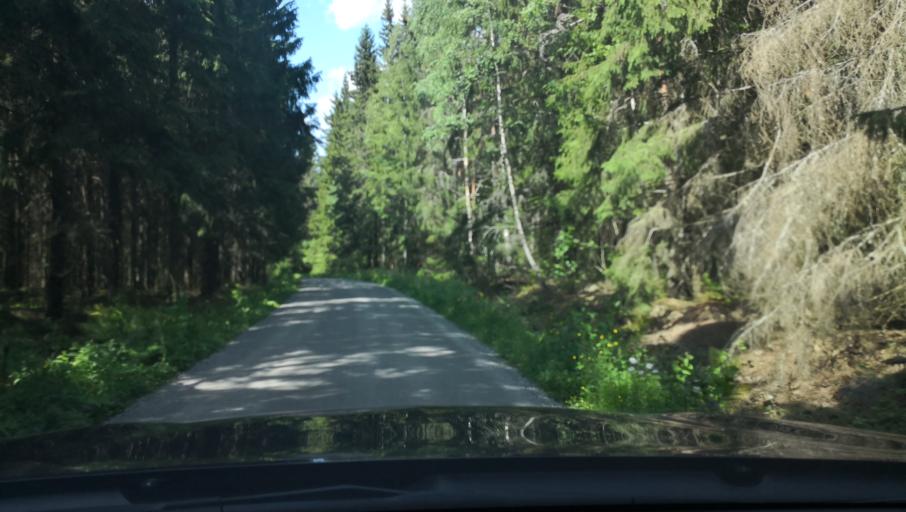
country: SE
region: Vaestmanland
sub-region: Surahammars Kommun
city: Ramnas
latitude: 59.8812
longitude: 16.0931
